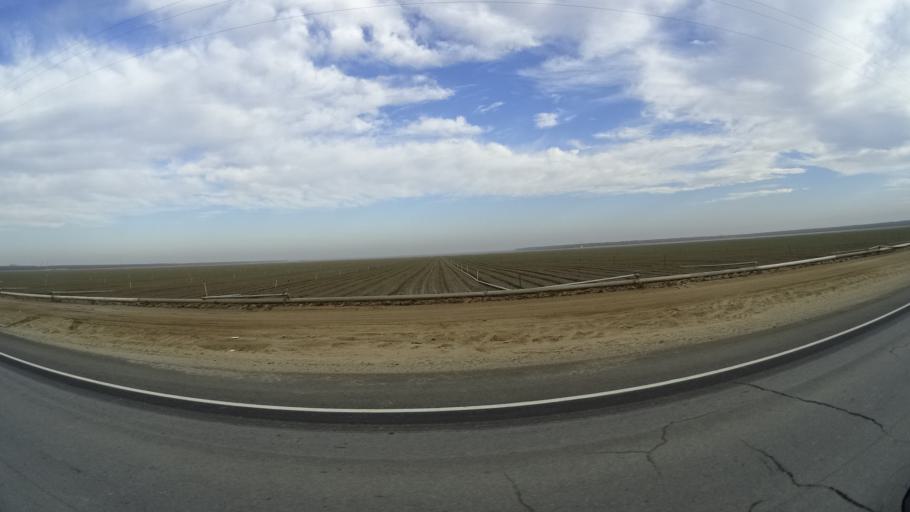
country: US
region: California
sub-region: Kern County
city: Rosedale
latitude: 35.4197
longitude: -119.2199
